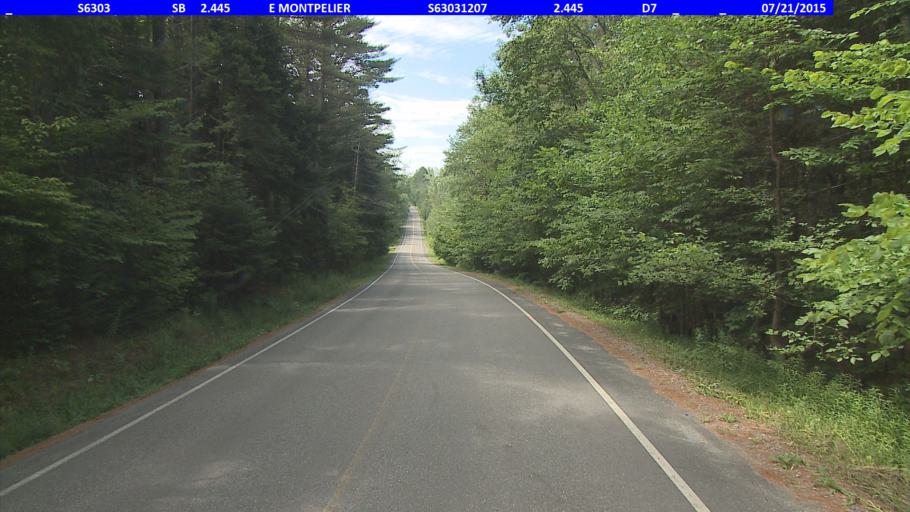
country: US
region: Vermont
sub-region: Washington County
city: Montpelier
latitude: 44.3031
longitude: -72.5326
